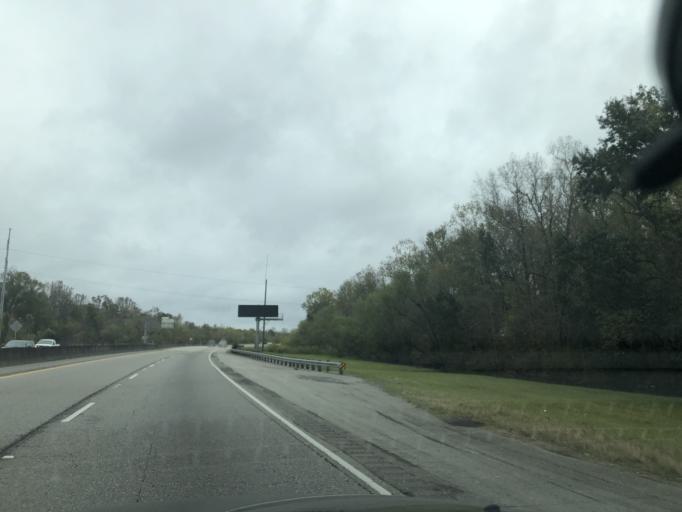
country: US
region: Louisiana
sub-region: Saint Charles Parish
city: Destrehan
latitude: 29.9584
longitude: -90.3646
